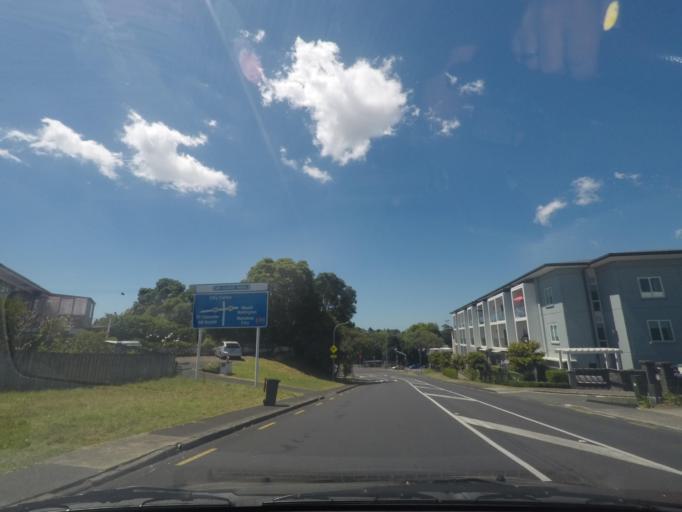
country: NZ
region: Auckland
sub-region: Auckland
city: Auckland
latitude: -36.9101
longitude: 174.7580
